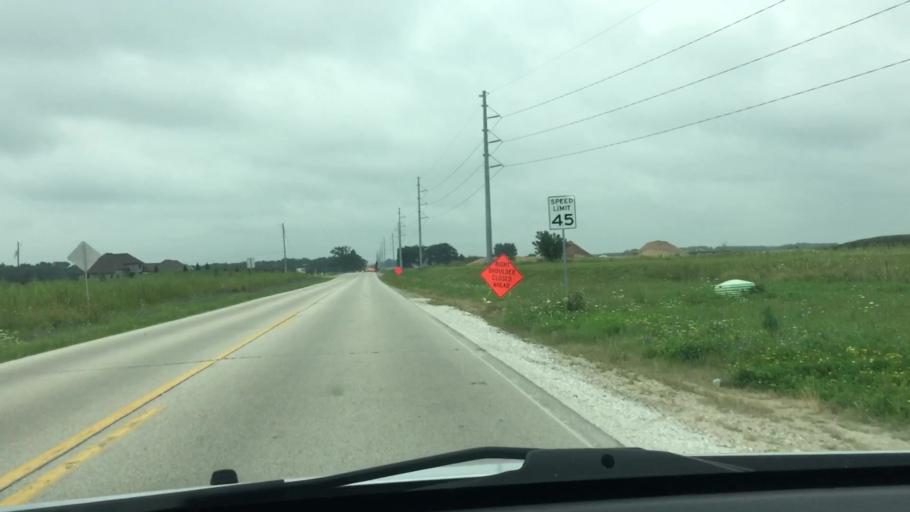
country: US
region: Wisconsin
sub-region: Waukesha County
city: Delafield
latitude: 43.0797
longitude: -88.4419
